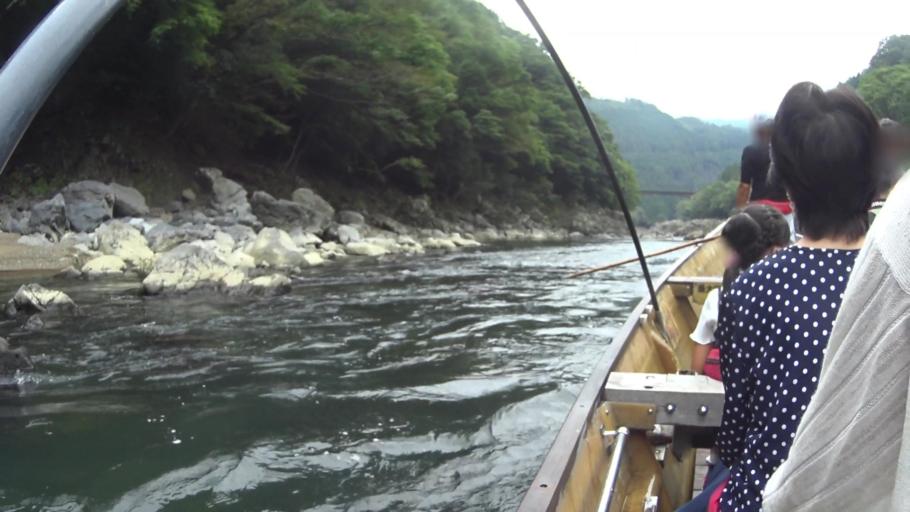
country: JP
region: Kyoto
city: Kameoka
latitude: 35.0188
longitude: 135.6259
